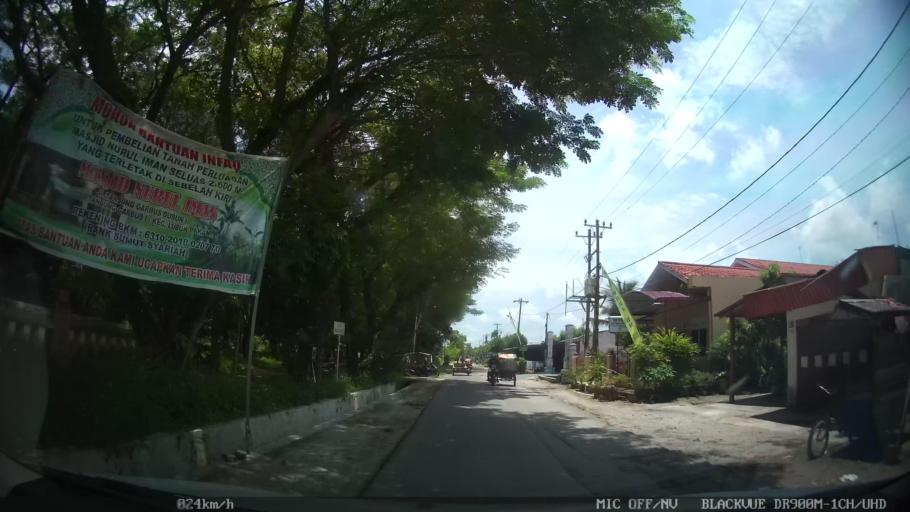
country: ID
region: North Sumatra
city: Percut
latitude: 3.5462
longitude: 98.8654
